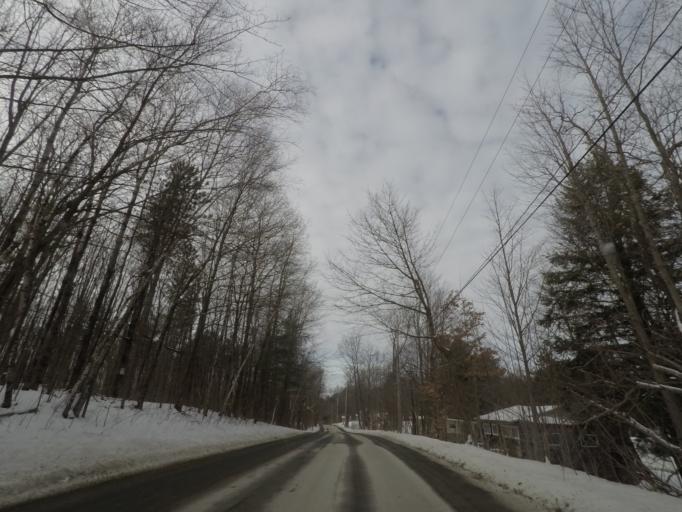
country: US
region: New York
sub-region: Rensselaer County
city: Averill Park
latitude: 42.6068
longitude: -73.5267
